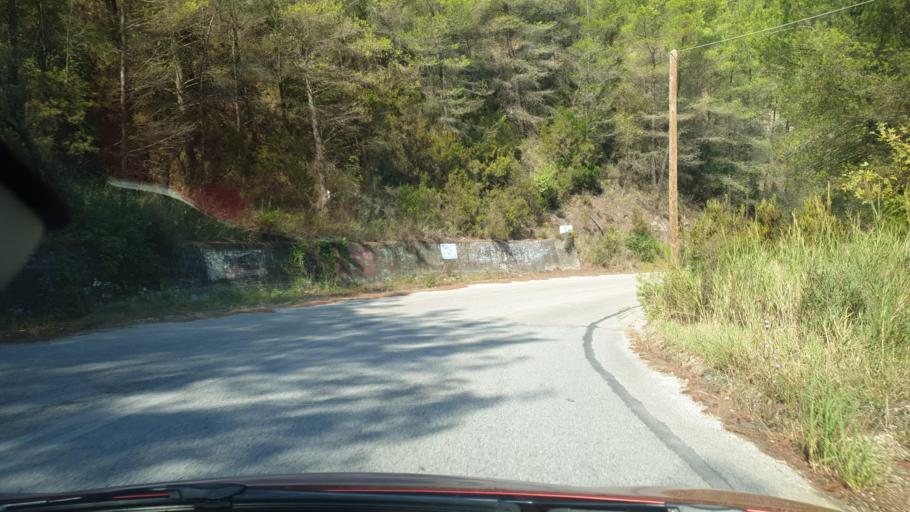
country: GR
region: Central Macedonia
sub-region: Nomos Chalkidikis
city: Neos Marmaras
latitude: 40.1738
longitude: 23.8362
